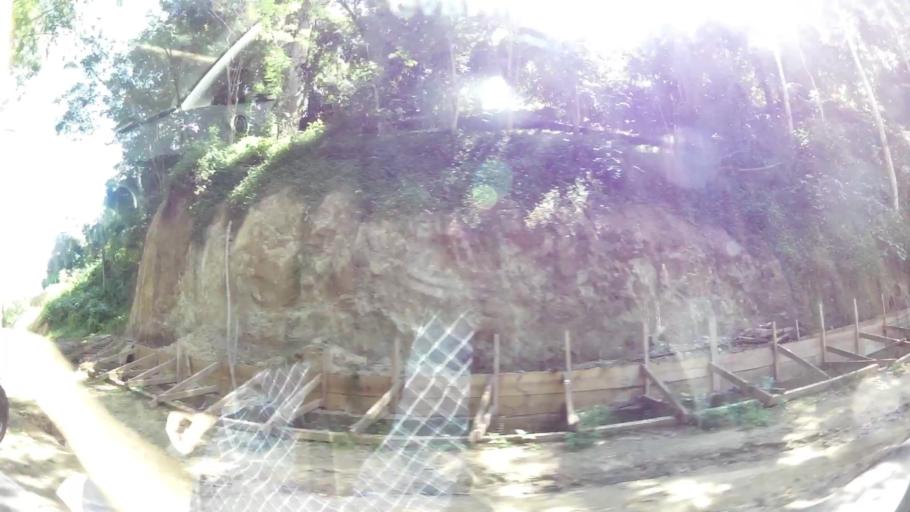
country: TT
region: Tobago
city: Scarborough
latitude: 11.2261
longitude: -60.7621
